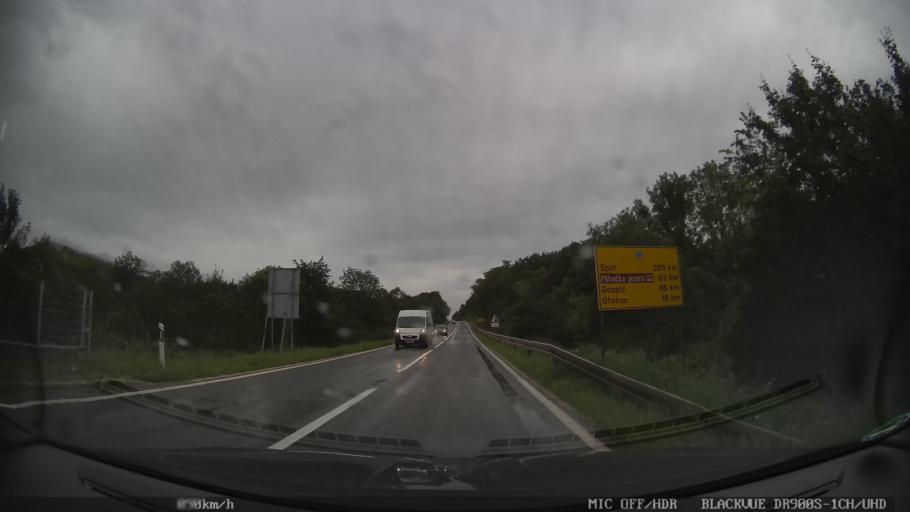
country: HR
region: Licko-Senjska
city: Brinje
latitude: 44.9639
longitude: 15.0800
